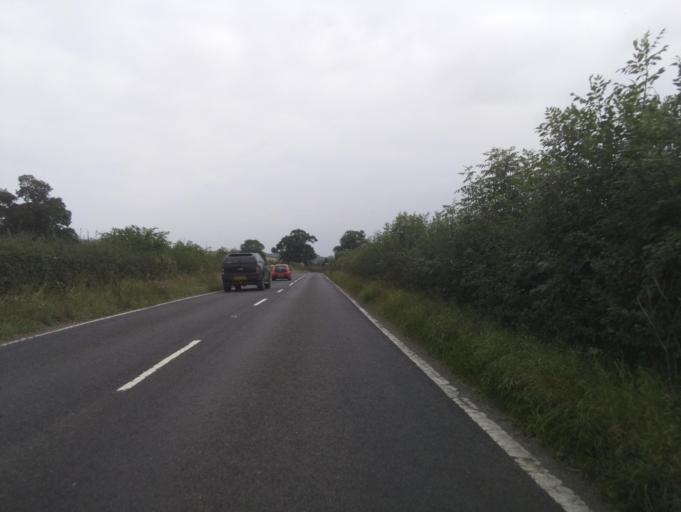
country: GB
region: England
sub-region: Derbyshire
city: Belper
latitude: 53.0217
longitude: -1.5473
